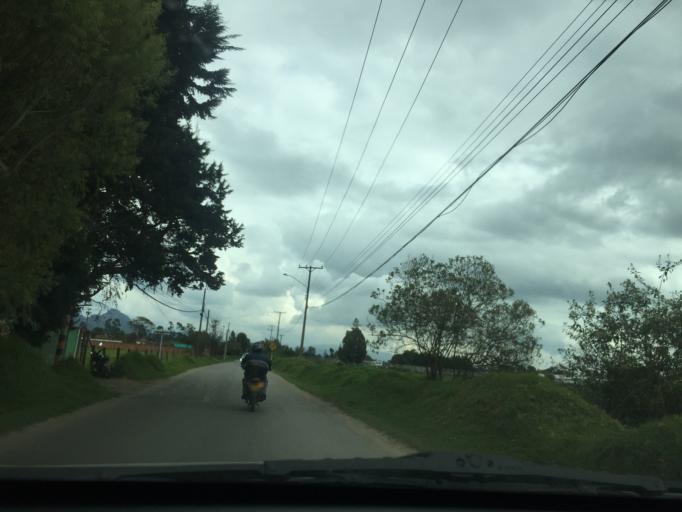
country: CO
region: Cundinamarca
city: Cota
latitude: 4.8121
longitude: -74.0748
